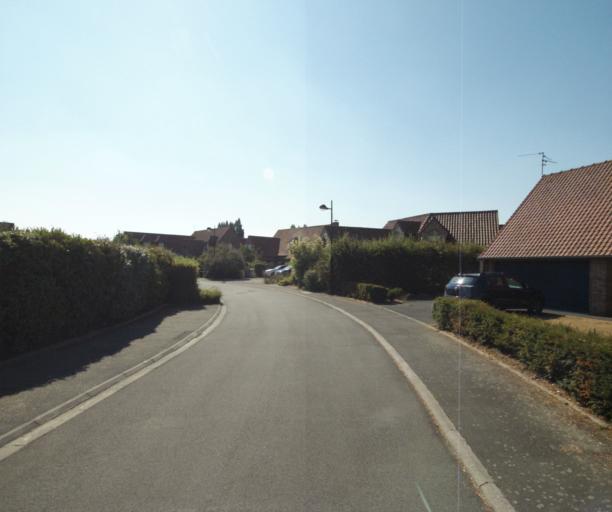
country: FR
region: Nord-Pas-de-Calais
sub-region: Departement du Nord
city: Wervicq-Sud
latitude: 50.7627
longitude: 3.0553
